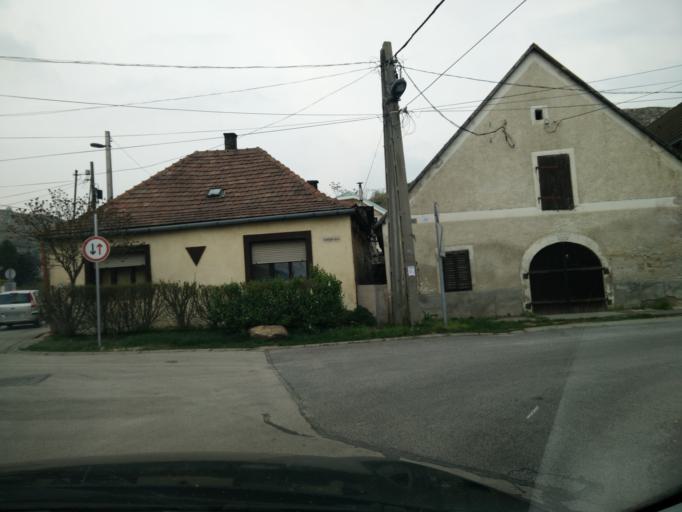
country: HU
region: Pest
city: Budaors
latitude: 47.4627
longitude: 18.9527
